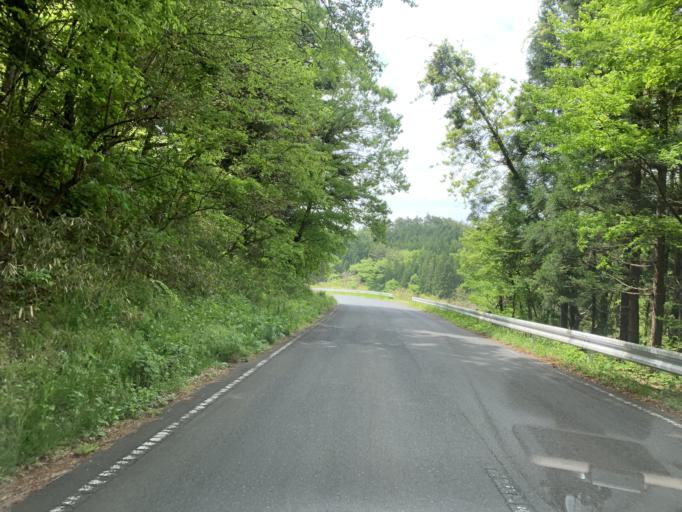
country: JP
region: Iwate
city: Ichinoseki
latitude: 38.8770
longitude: 140.9759
